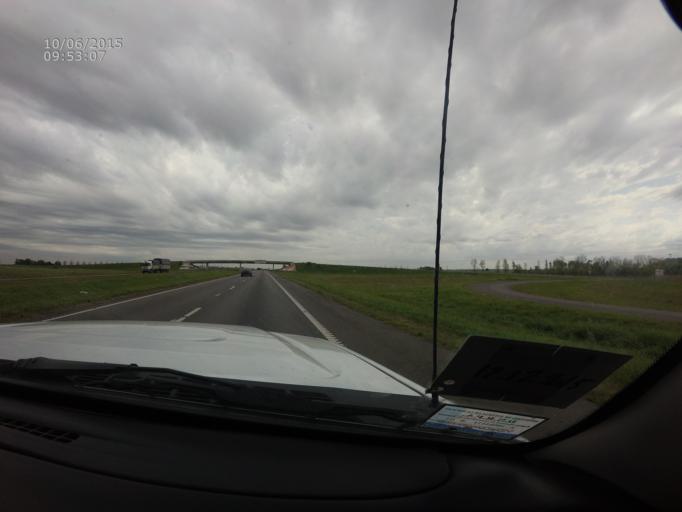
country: AR
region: Buenos Aires
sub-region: Partido de Baradero
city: Baradero
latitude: -33.9793
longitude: -59.3786
